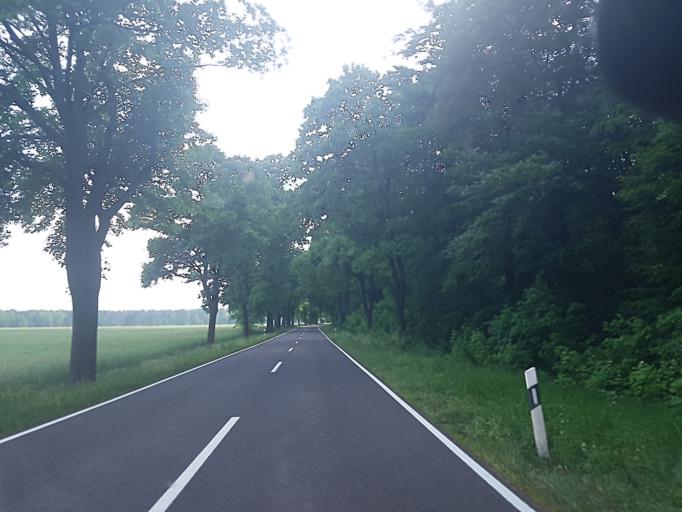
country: DE
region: Brandenburg
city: Gorzke
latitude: 52.0611
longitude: 12.2915
